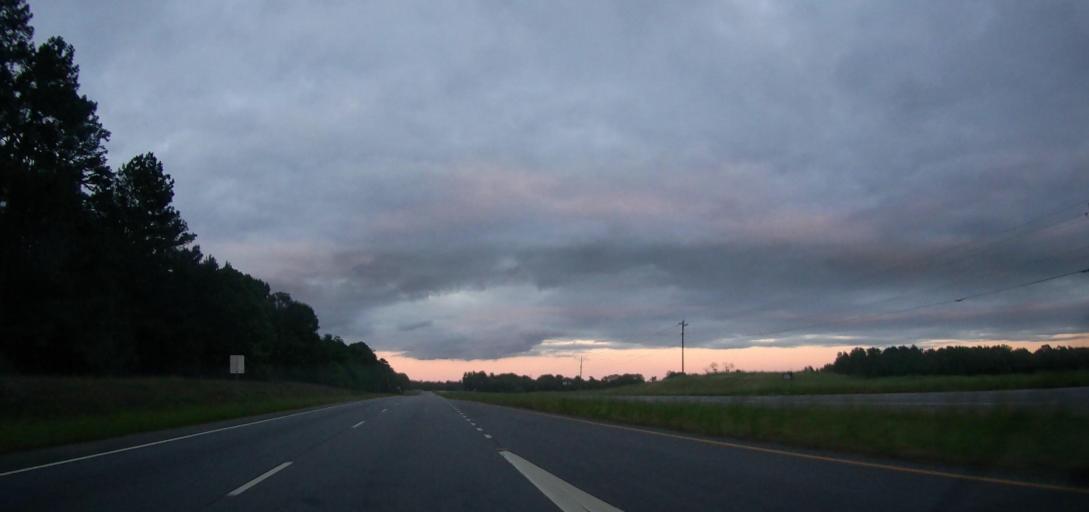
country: US
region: Georgia
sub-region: Jackson County
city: Arcade
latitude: 34.0618
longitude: -83.5226
